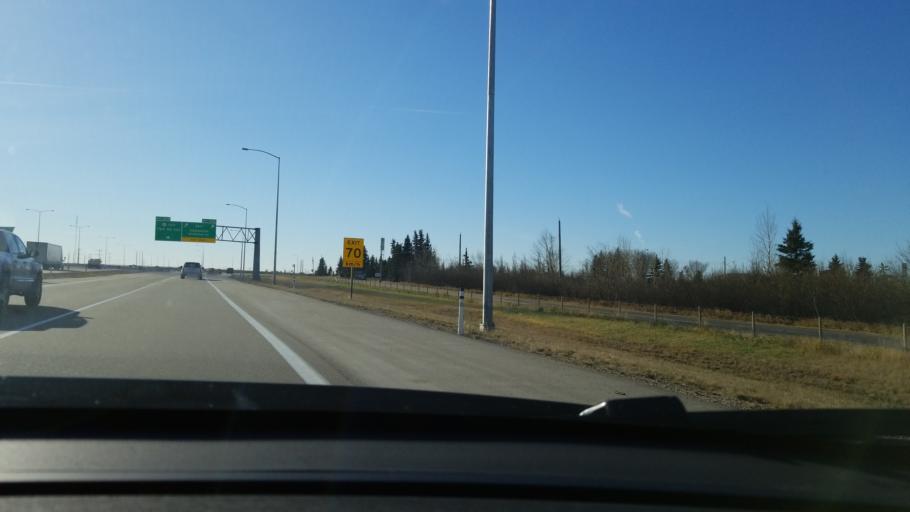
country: CA
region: Alberta
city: Sherwood Park
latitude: 53.4904
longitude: -113.3439
